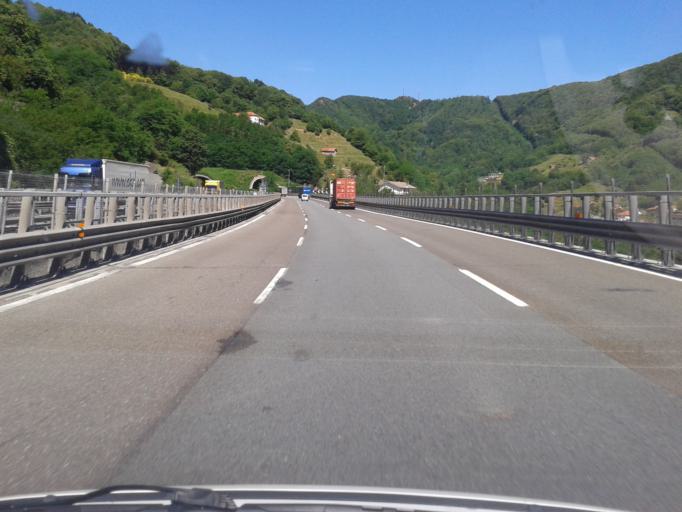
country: IT
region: Liguria
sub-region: Provincia di Genova
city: Campo Ligure
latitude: 44.5390
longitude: 8.6945
